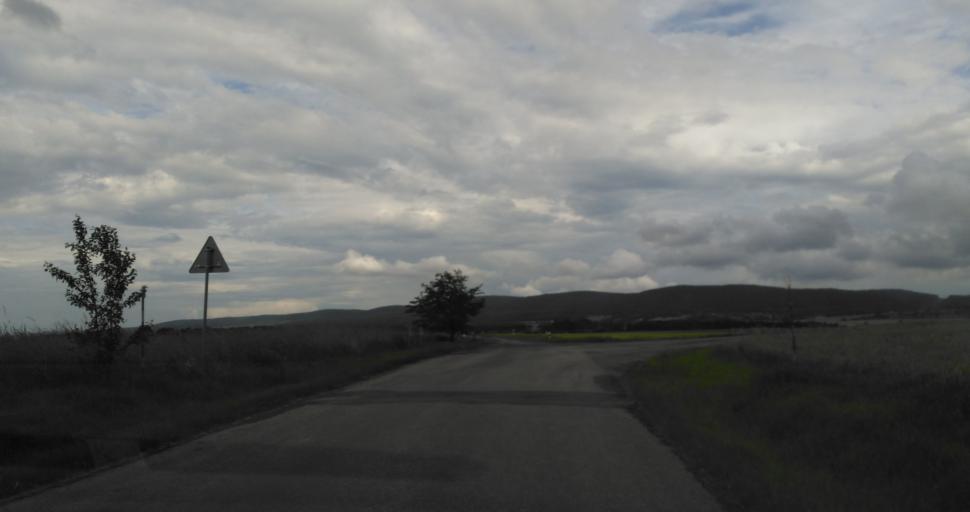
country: CZ
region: Central Bohemia
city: Hostomice
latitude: 49.8468
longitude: 14.0443
